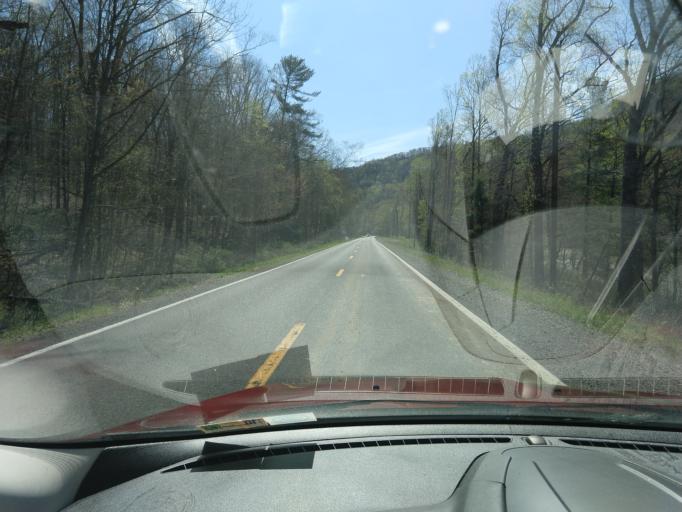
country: US
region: West Virginia
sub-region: Greenbrier County
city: Alderson
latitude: 37.7204
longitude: -80.6247
